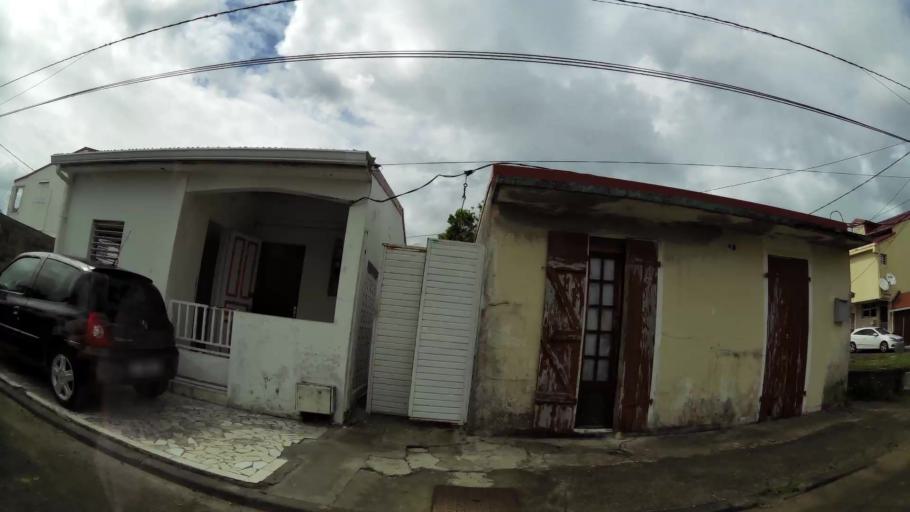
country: GP
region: Guadeloupe
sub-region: Guadeloupe
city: Baie-Mahault
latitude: 16.2667
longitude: -61.5855
